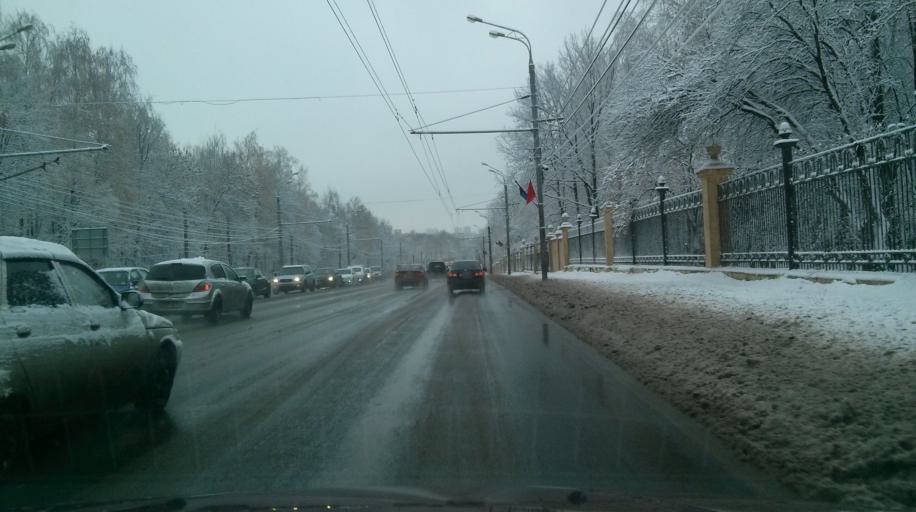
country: RU
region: Nizjnij Novgorod
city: Nizhniy Novgorod
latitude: 56.2661
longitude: 43.9748
